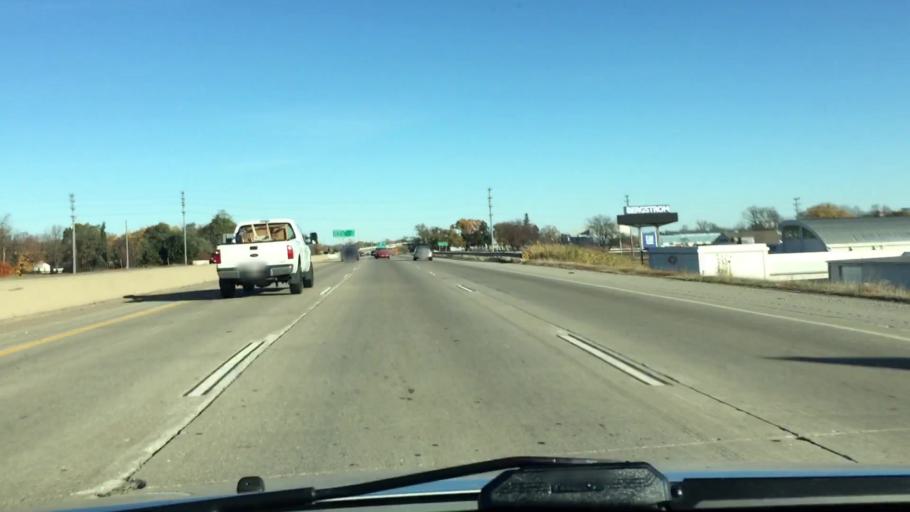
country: US
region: Wisconsin
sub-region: Winnebago County
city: Neenah
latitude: 44.1911
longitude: -88.4873
